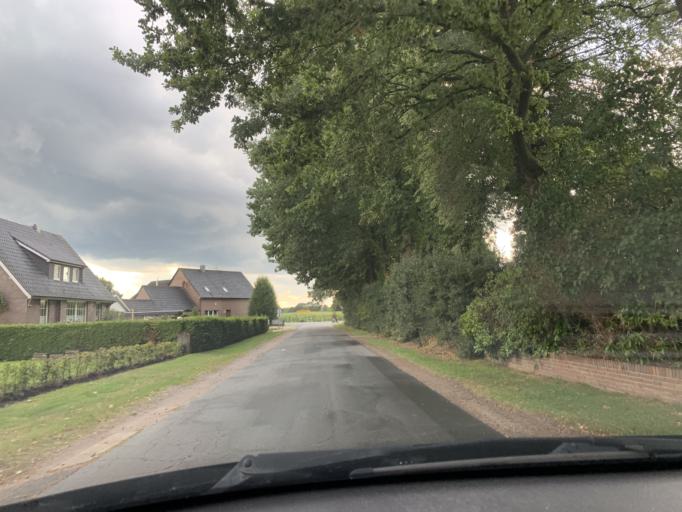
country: DE
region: Lower Saxony
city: Westerstede
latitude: 53.3065
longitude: 7.9679
